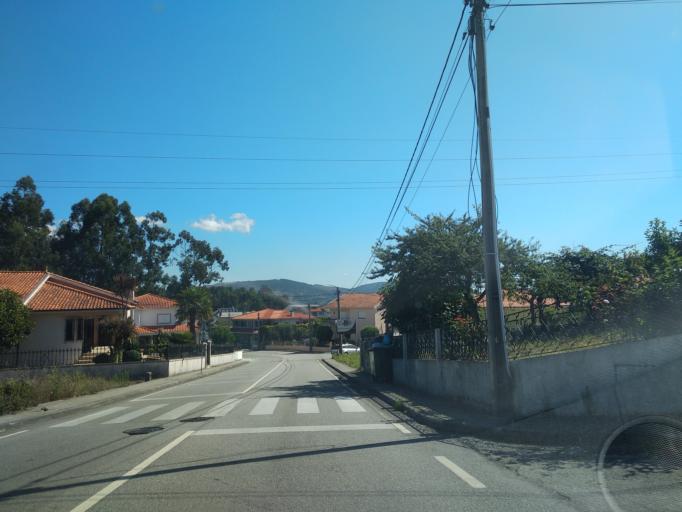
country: PT
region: Porto
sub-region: Pacos de Ferreira
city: Ferreira
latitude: 41.2720
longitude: -8.3358
